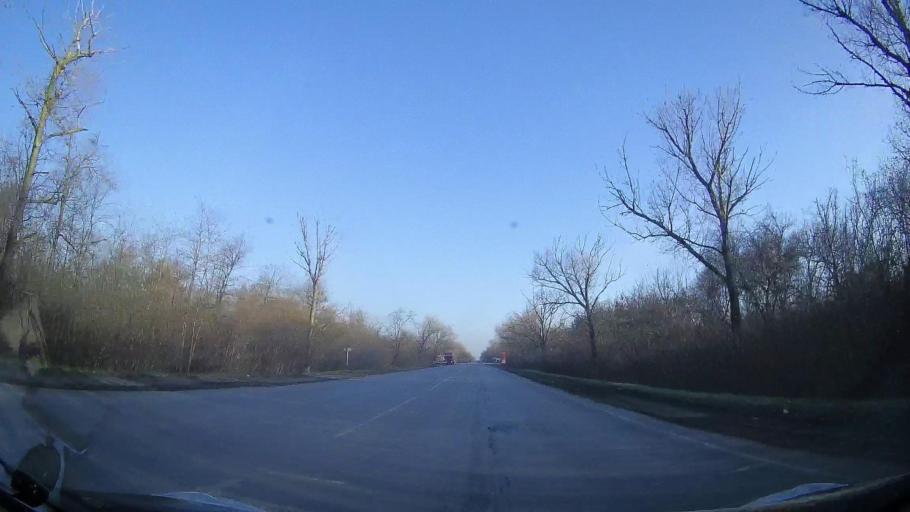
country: RU
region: Rostov
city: Bataysk
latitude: 47.0498
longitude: 39.8391
